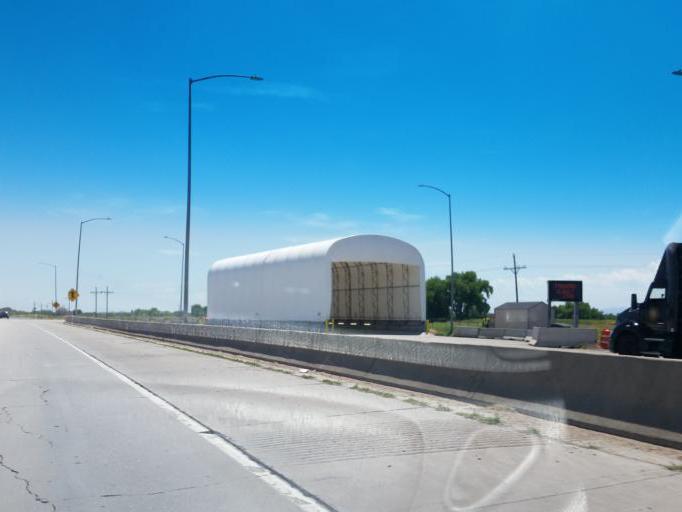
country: US
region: Colorado
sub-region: Larimer County
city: Fort Collins
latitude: 40.5566
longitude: -105.0010
